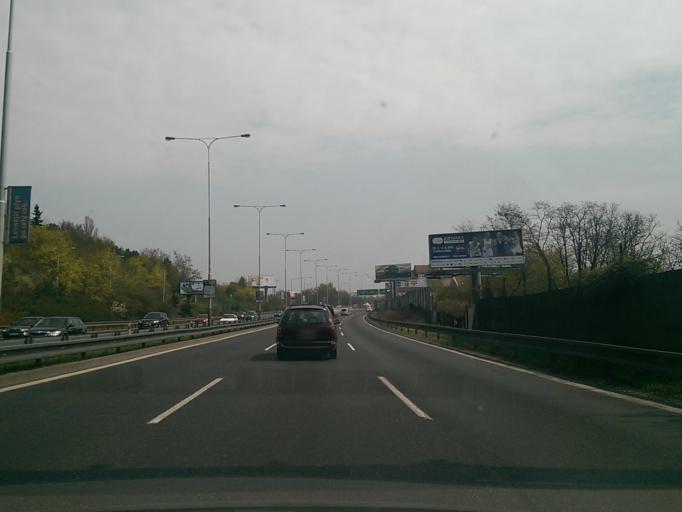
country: CZ
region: Praha
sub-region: Praha 4
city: Hodkovicky
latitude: 50.0376
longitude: 14.4519
